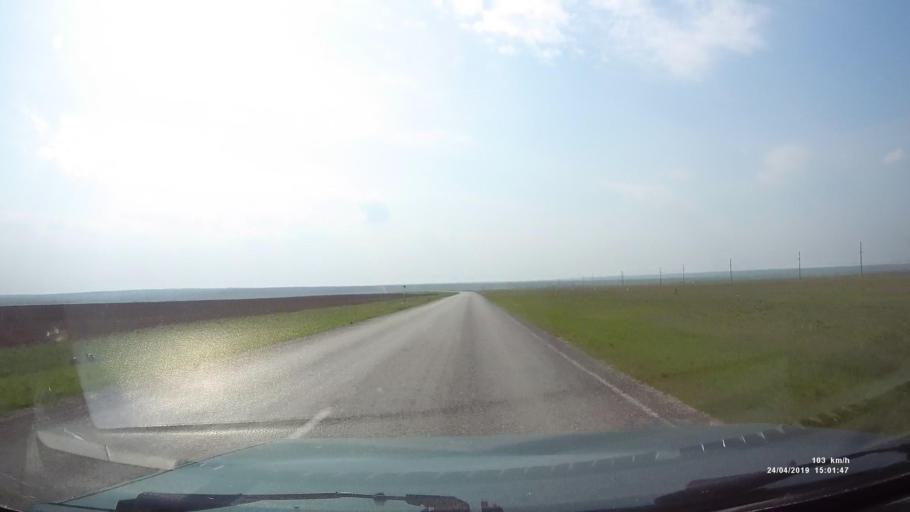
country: RU
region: Rostov
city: Remontnoye
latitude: 46.5664
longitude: 43.5267
